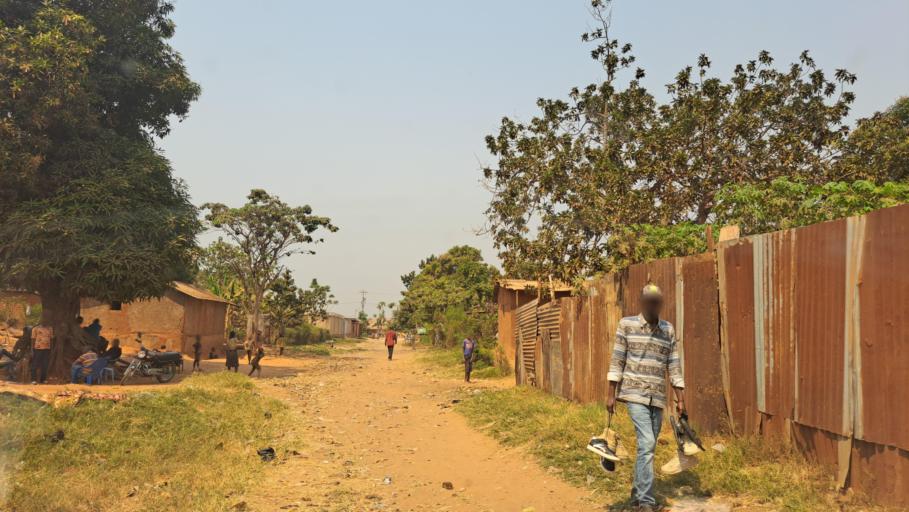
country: CD
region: Kasai-Oriental
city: Mbuji-Mayi
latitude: -6.1262
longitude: 23.6134
